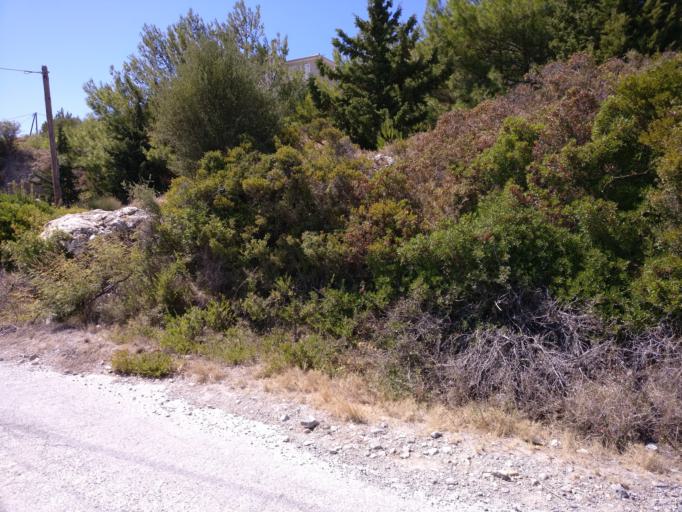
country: GR
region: North Aegean
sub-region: Nomos Samou
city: Pythagoreio
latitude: 37.7016
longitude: 26.9669
